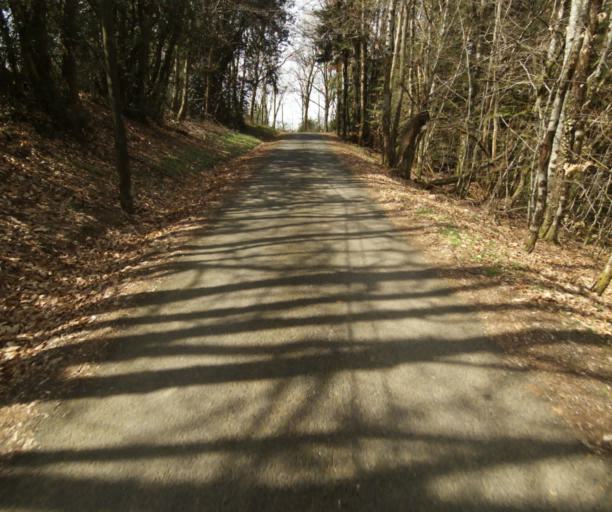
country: FR
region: Limousin
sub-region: Departement de la Correze
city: Correze
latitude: 45.3819
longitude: 1.8028
